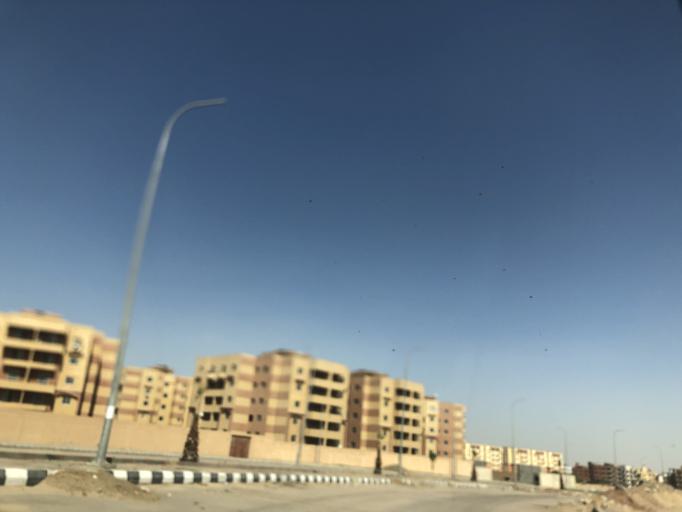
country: EG
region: Al Jizah
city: Madinat Sittah Uktubar
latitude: 29.9265
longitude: 31.0413
